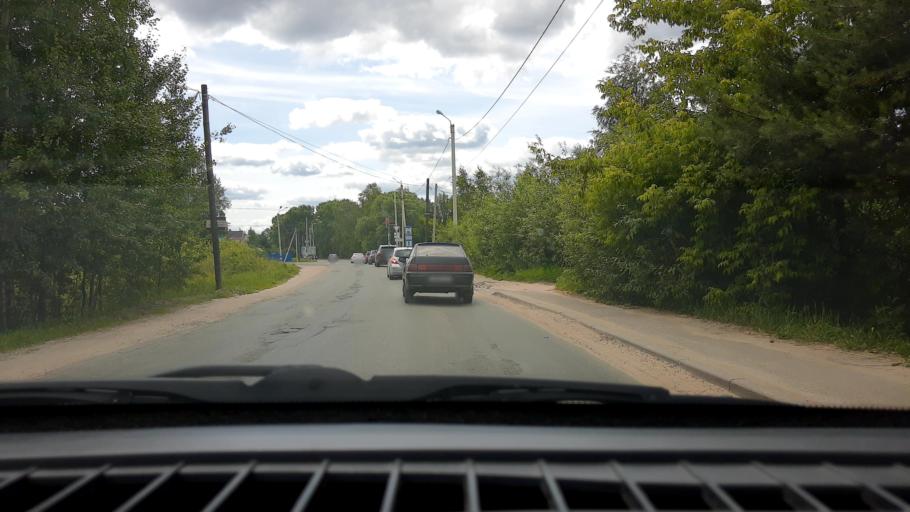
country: RU
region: Nizjnij Novgorod
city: Bor
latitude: 56.3830
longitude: 44.0373
